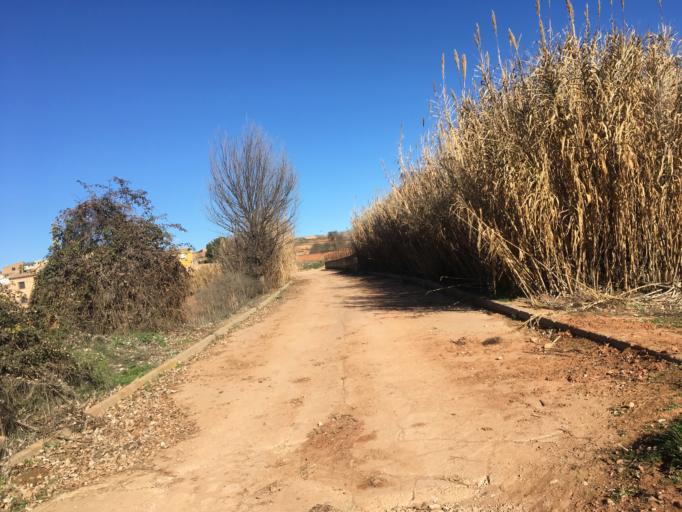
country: ES
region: Castille-La Mancha
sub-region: Provincia de Cuenca
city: Atalaya del Canavate
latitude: 39.5464
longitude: -2.2472
